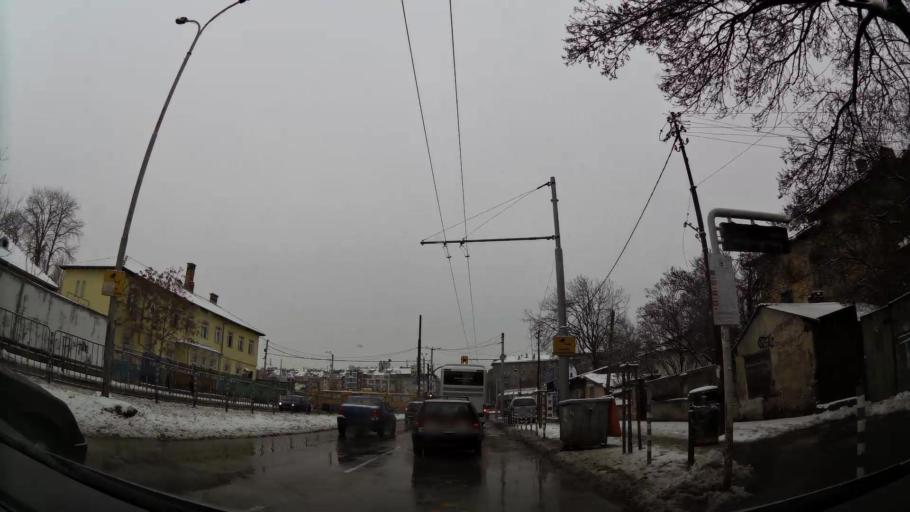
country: BG
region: Sofia-Capital
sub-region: Stolichna Obshtina
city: Sofia
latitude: 42.7059
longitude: 23.3325
